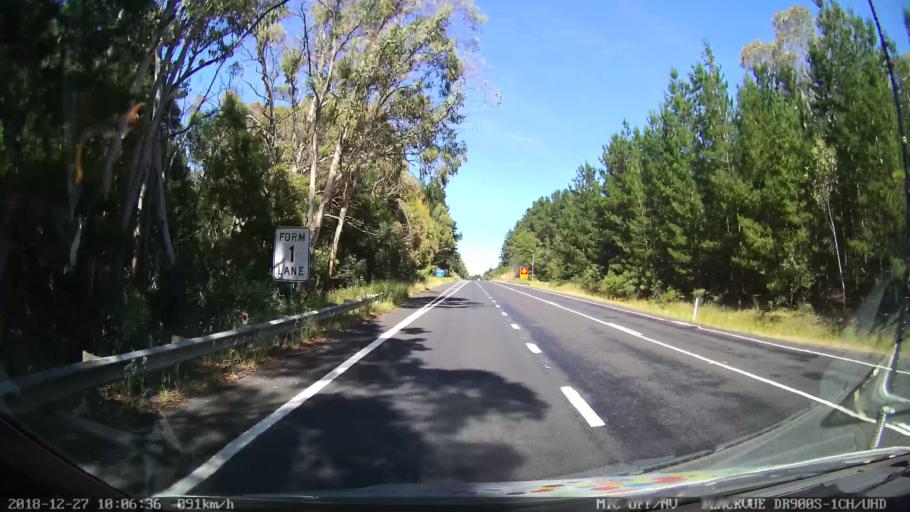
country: AU
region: New South Wales
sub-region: Lithgow
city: Portland
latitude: -33.4374
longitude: 149.8526
